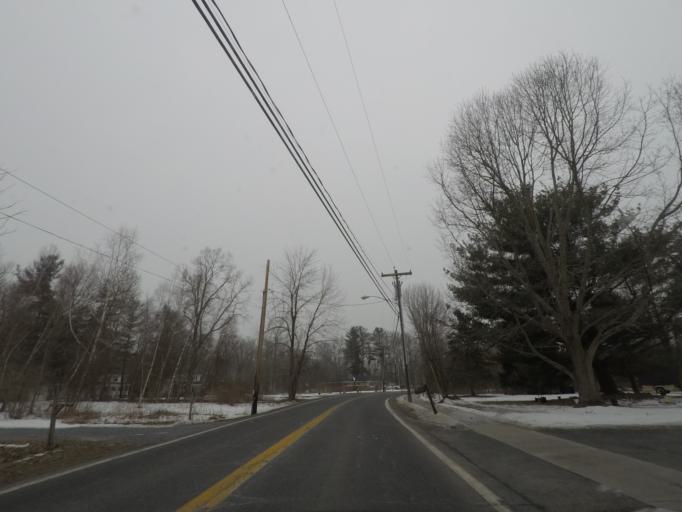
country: US
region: New York
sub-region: Rensselaer County
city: Castleton-on-Hudson
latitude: 42.5430
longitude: -73.8025
